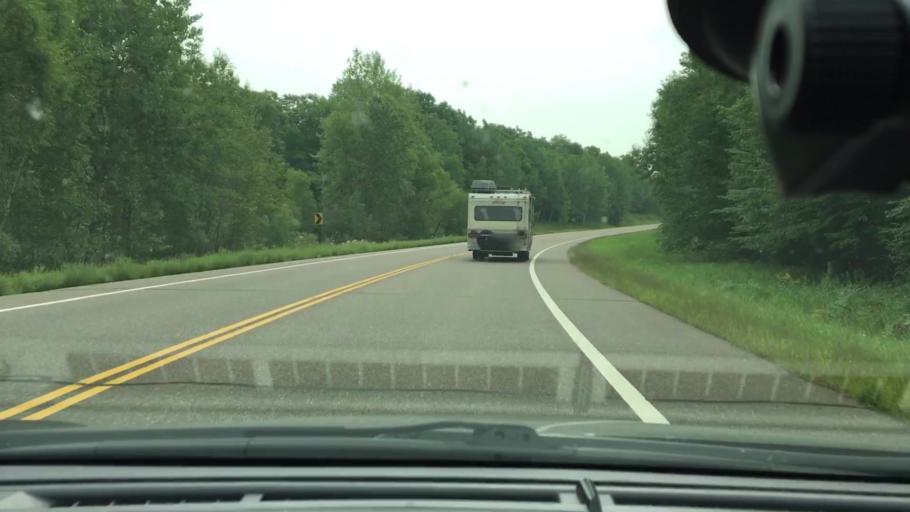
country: US
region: Minnesota
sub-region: Crow Wing County
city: Crosby
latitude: 46.4110
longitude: -93.8253
